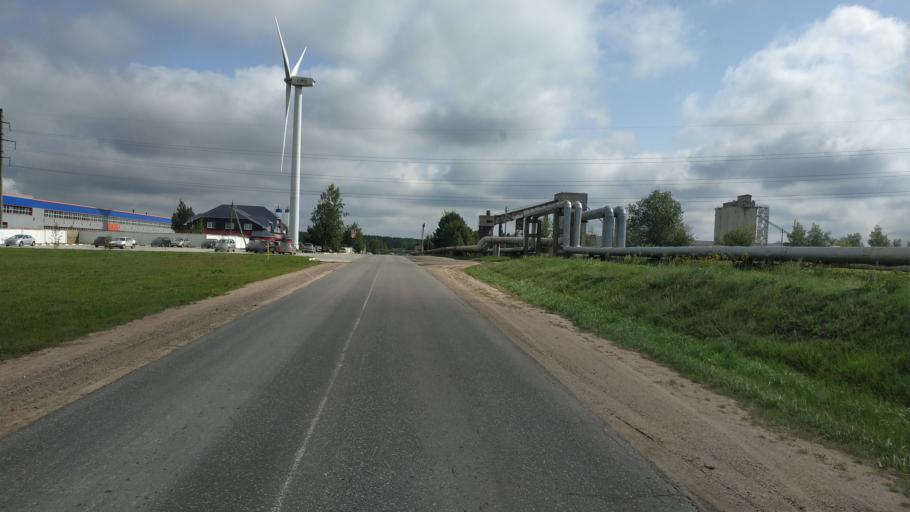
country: BY
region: Mogilev
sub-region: Mahilyowski Rayon
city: Veyno
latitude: 53.8398
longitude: 30.3762
